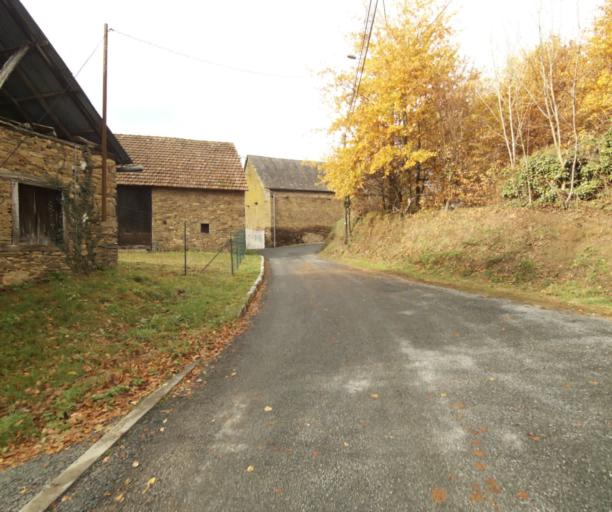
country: FR
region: Limousin
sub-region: Departement de la Correze
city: Sainte-Fereole
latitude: 45.2102
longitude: 1.6273
